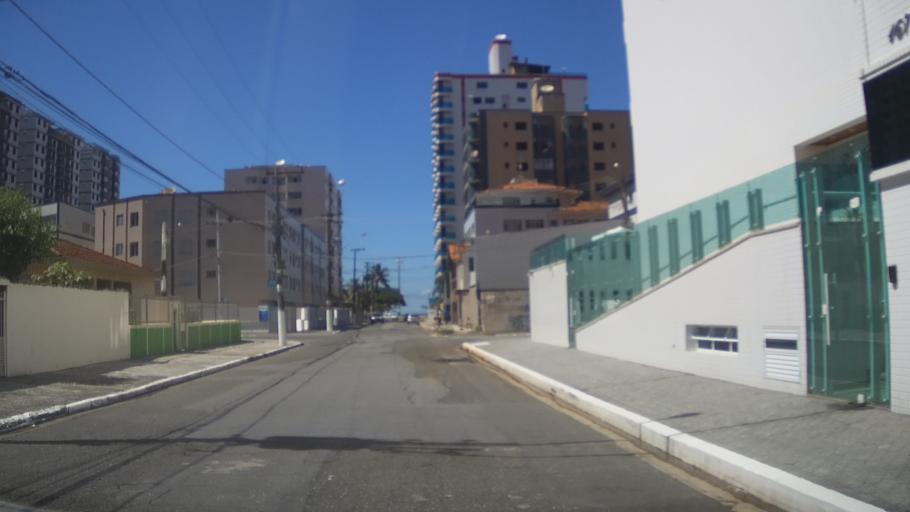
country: BR
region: Sao Paulo
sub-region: Praia Grande
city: Praia Grande
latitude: -24.0251
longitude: -46.4660
